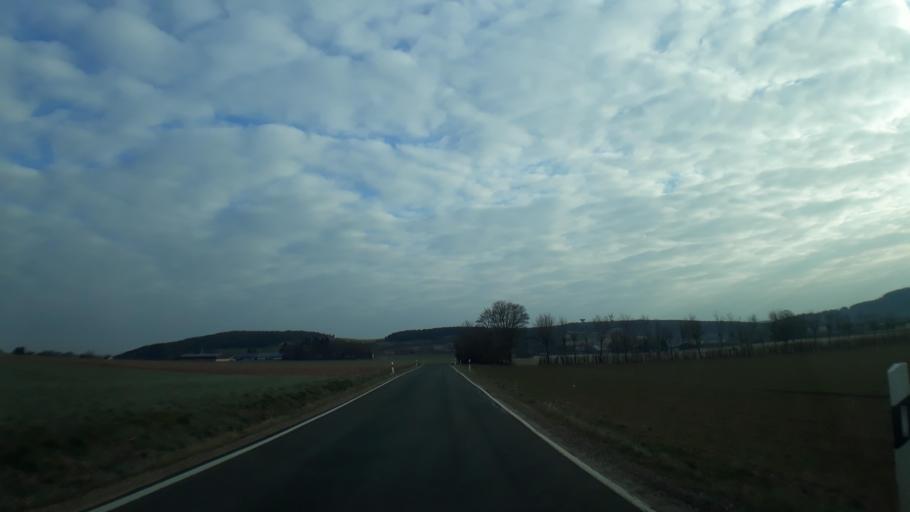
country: DE
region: North Rhine-Westphalia
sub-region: Regierungsbezirk Koln
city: Mechernich
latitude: 50.5598
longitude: 6.6929
